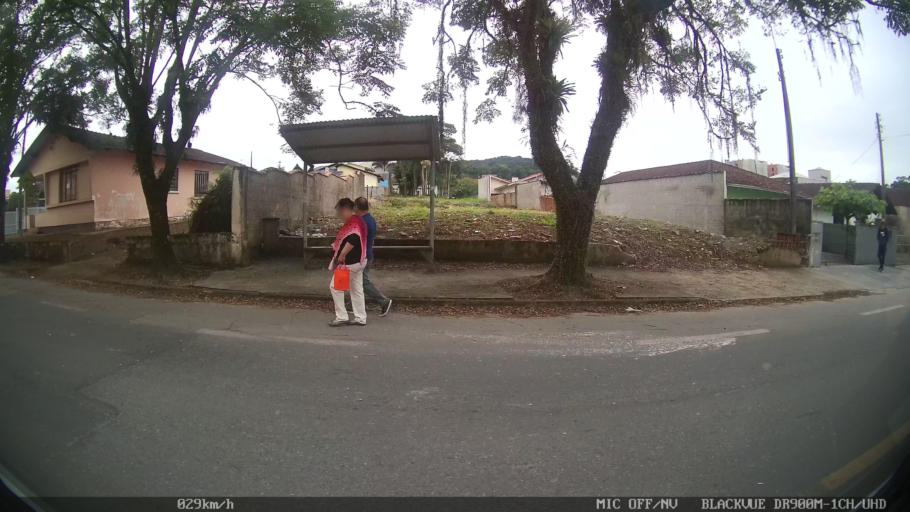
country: BR
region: Santa Catarina
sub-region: Joinville
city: Joinville
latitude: -26.2733
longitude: -48.8404
